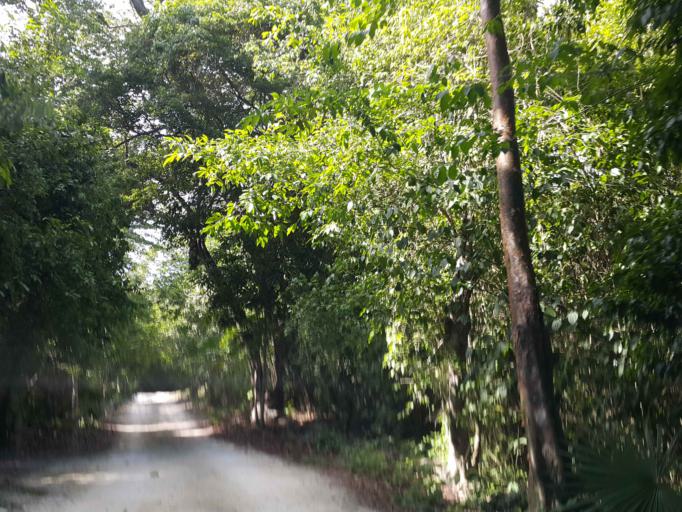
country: MX
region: Quintana Roo
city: Leona Vicario
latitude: 20.8702
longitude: -87.0457
